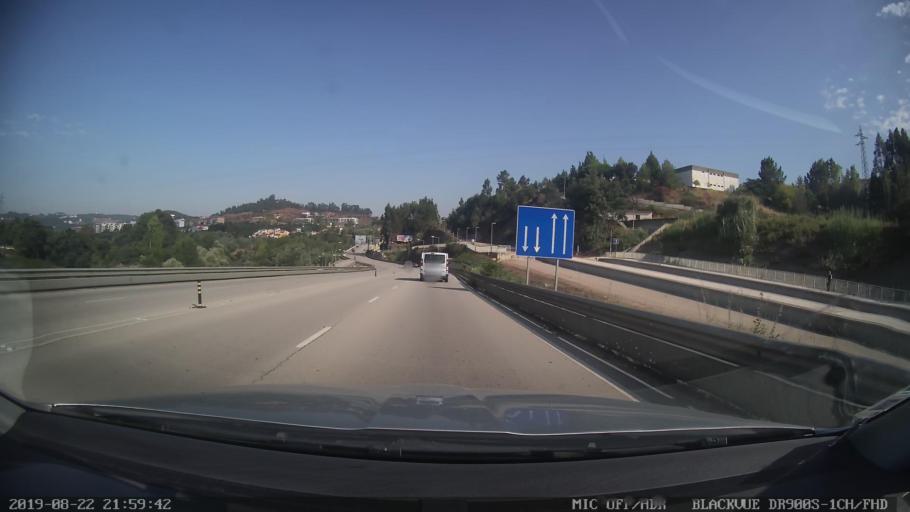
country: PT
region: Coimbra
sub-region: Coimbra
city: Coimbra
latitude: 40.1817
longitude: -8.3934
